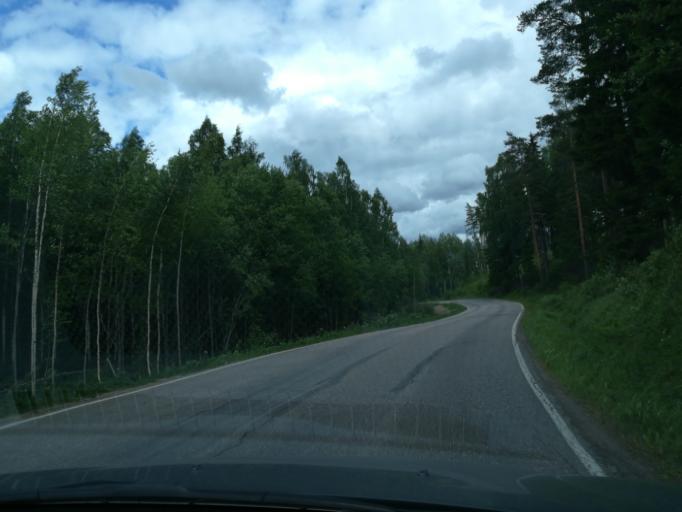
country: FI
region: South Karelia
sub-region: Lappeenranta
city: Savitaipale
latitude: 61.2197
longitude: 27.6955
